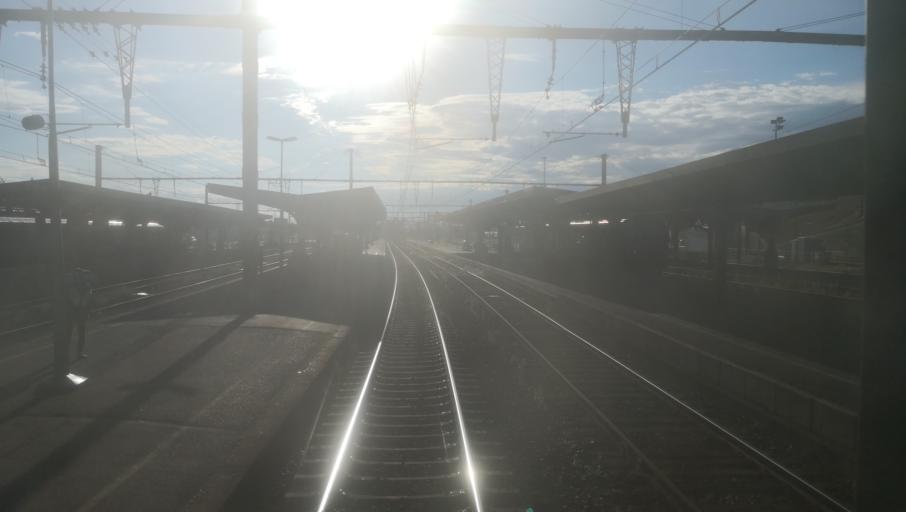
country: FR
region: Centre
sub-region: Departement du Cher
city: Vierzon
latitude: 47.2266
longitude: 2.0611
